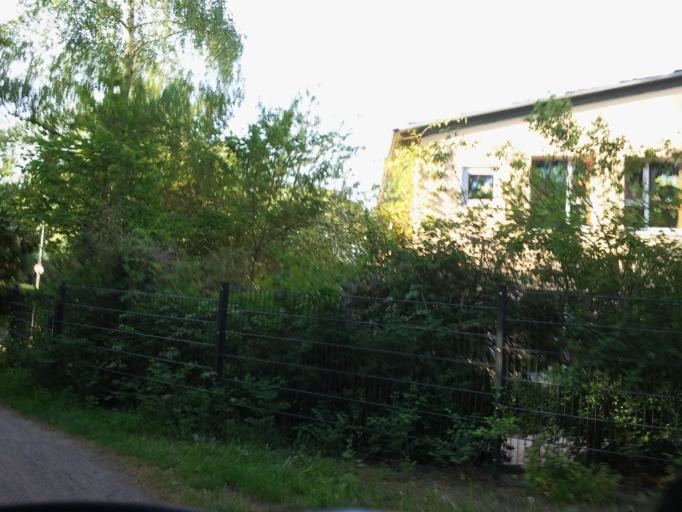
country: DE
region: Lower Saxony
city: Nienburg
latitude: 52.6377
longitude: 9.2189
